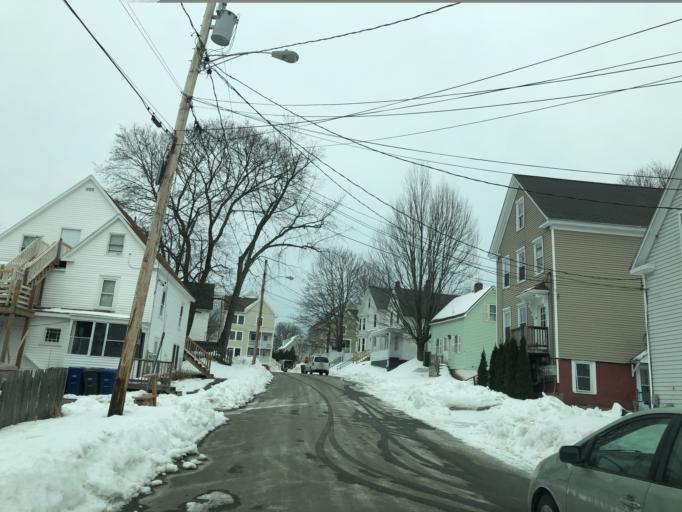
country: US
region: Maine
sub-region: Cumberland County
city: Westbrook
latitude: 43.6796
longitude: -70.3631
